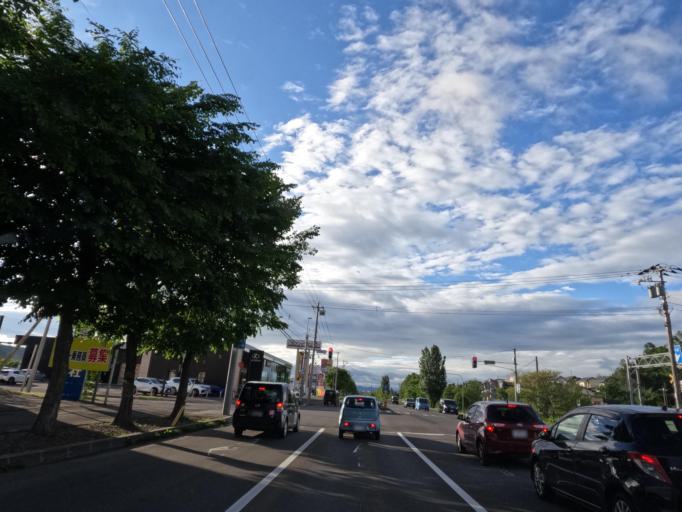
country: JP
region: Hokkaido
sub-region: Asahikawa-shi
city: Asahikawa
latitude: 43.7303
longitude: 142.3657
